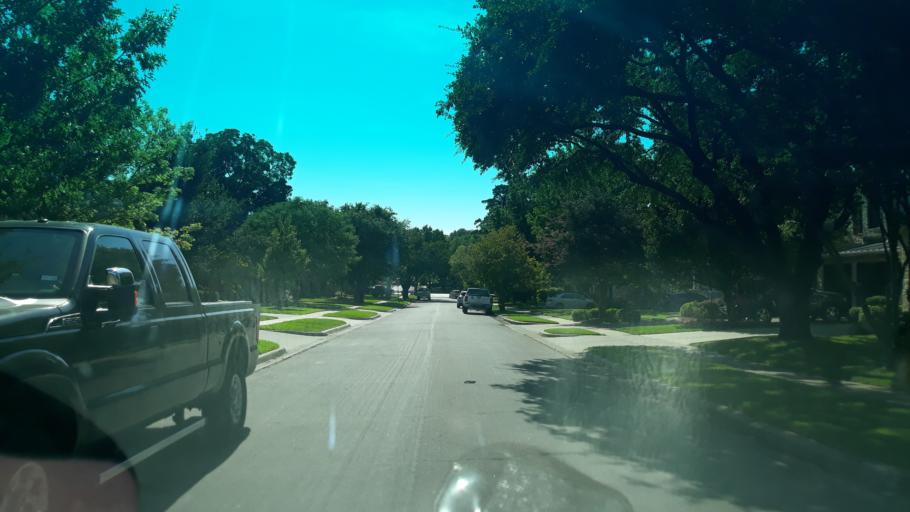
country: US
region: Texas
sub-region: Dallas County
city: Highland Park
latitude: 32.8211
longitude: -96.7596
